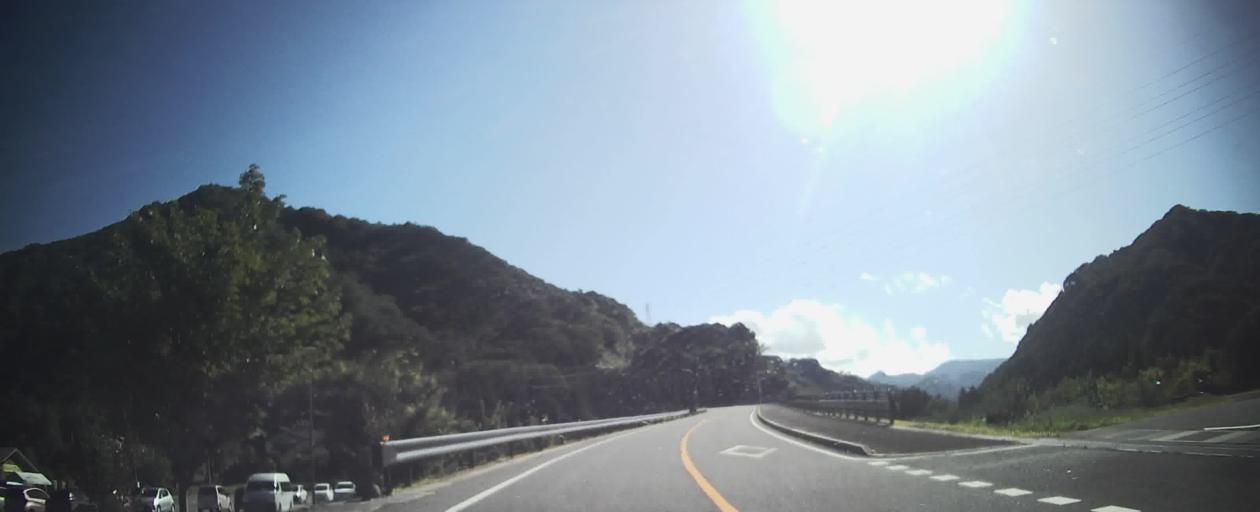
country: JP
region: Gunma
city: Nakanojomachi
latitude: 36.5694
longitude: 138.7344
